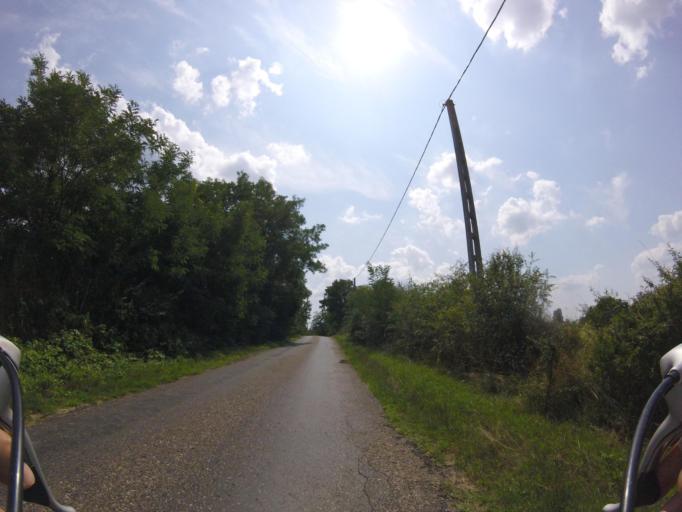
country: SK
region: Nitriansky
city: Sahy
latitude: 47.9899
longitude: 18.8149
